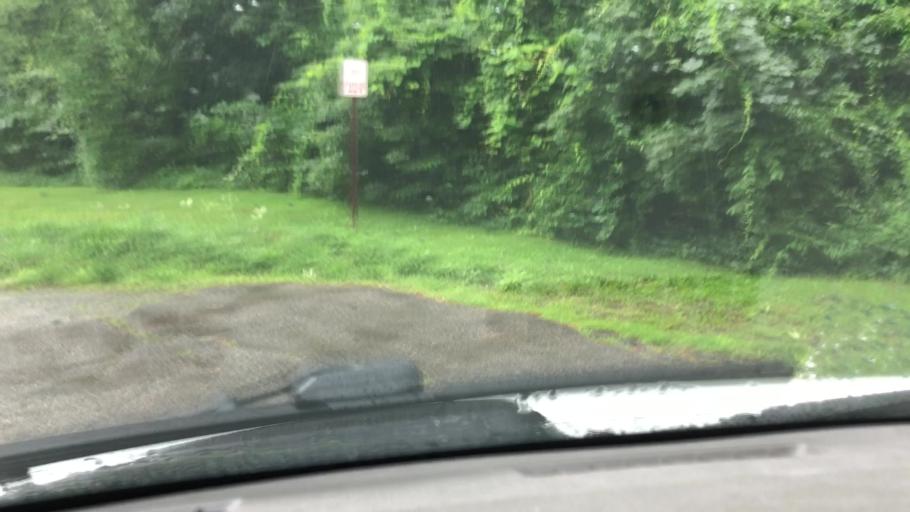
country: US
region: Massachusetts
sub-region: Berkshire County
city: Adams
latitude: 42.6238
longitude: -73.1121
